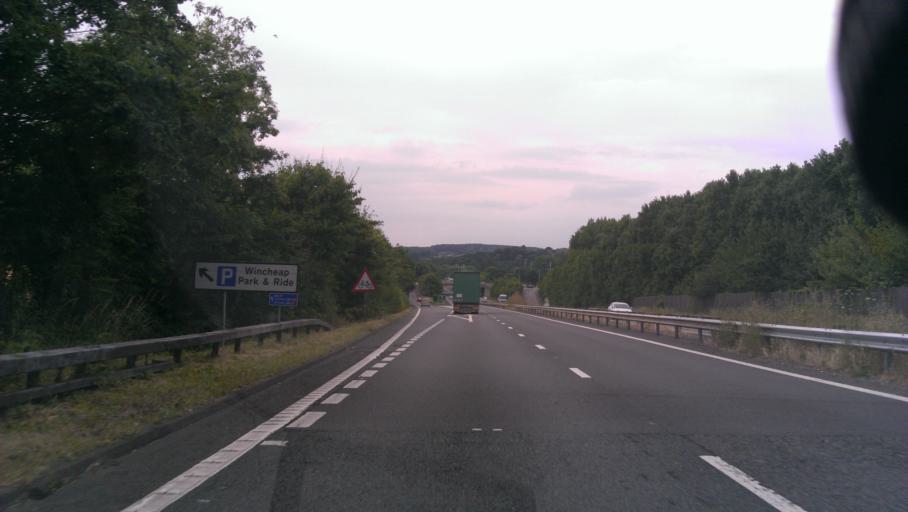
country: GB
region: England
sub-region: Kent
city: Canterbury
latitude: 51.2663
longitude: 1.0670
